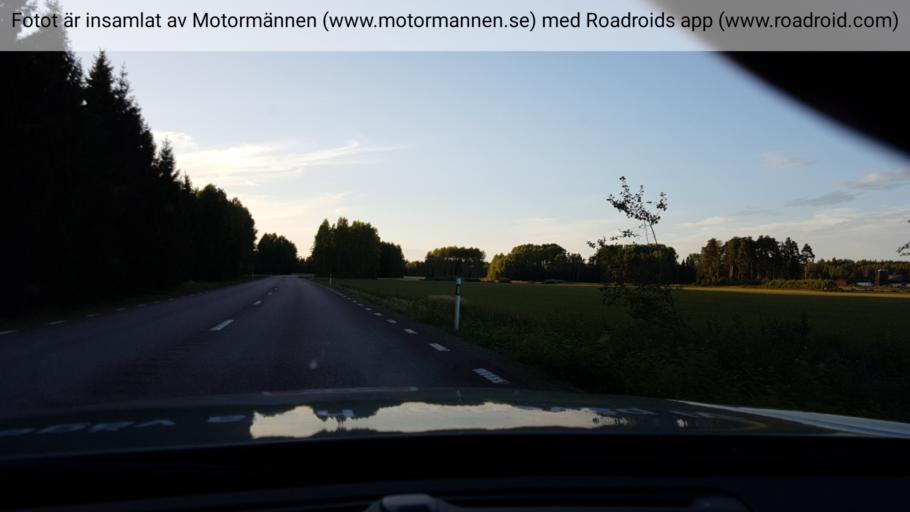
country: SE
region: OErebro
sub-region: Karlskoga Kommun
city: Karlskoga
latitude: 59.4066
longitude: 14.4302
